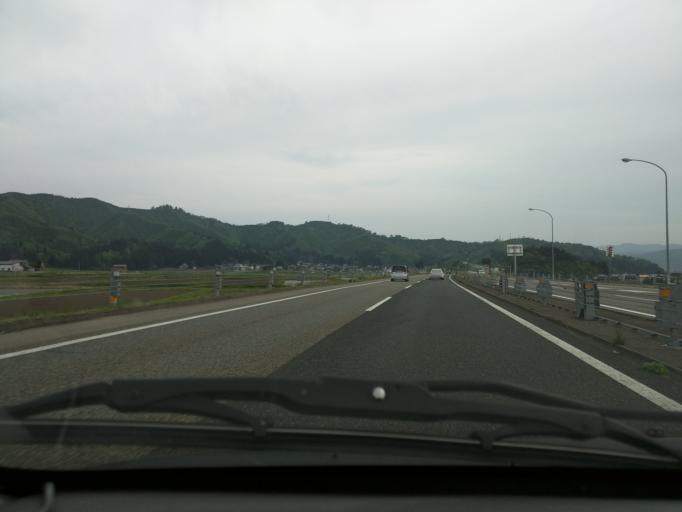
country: JP
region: Niigata
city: Muikamachi
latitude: 37.2125
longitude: 138.9728
